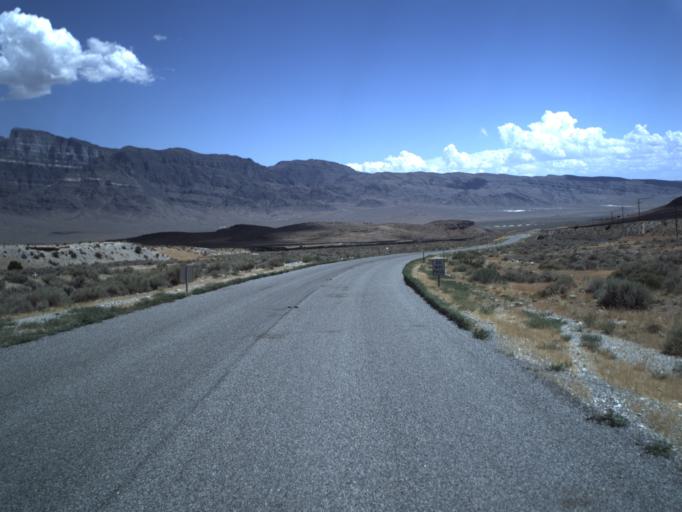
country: US
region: Utah
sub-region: Beaver County
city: Milford
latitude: 39.0879
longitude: -113.5529
